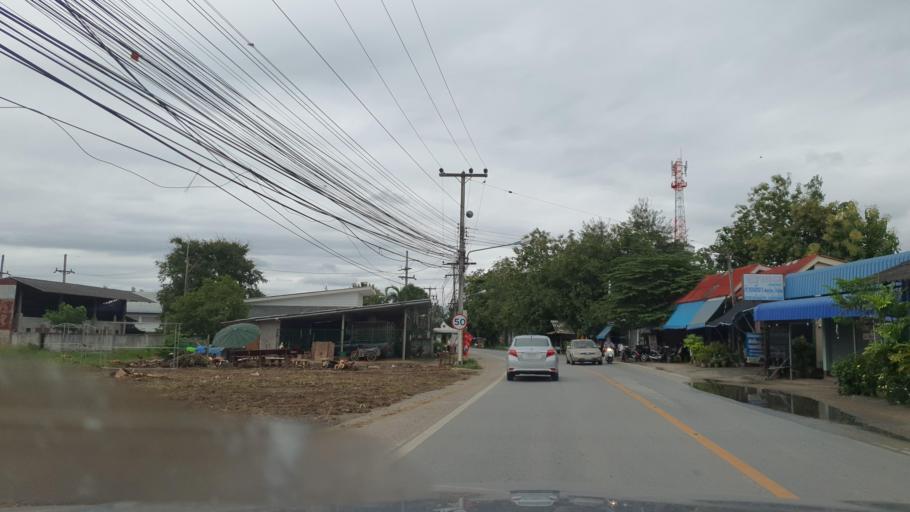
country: TH
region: Chiang Mai
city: San Pa Tong
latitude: 18.6241
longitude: 98.9317
